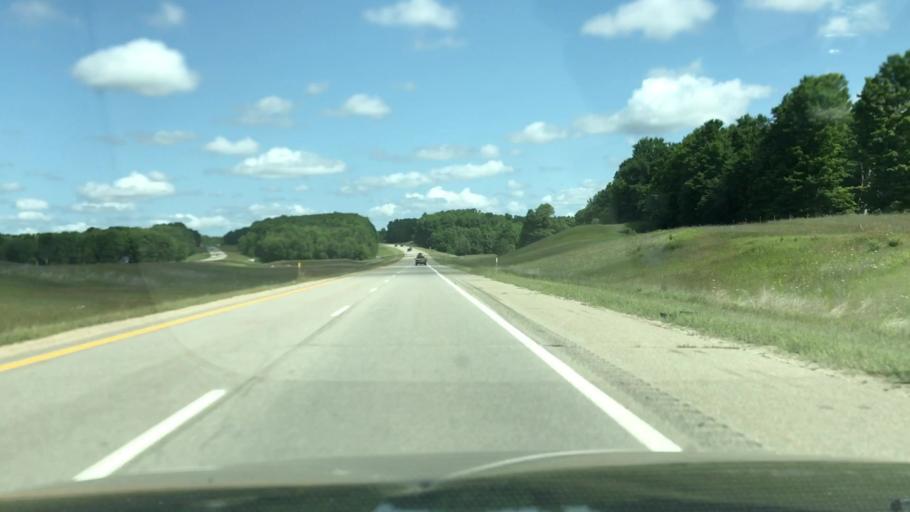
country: US
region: Michigan
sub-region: Osceola County
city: Reed City
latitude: 43.8001
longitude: -85.5337
